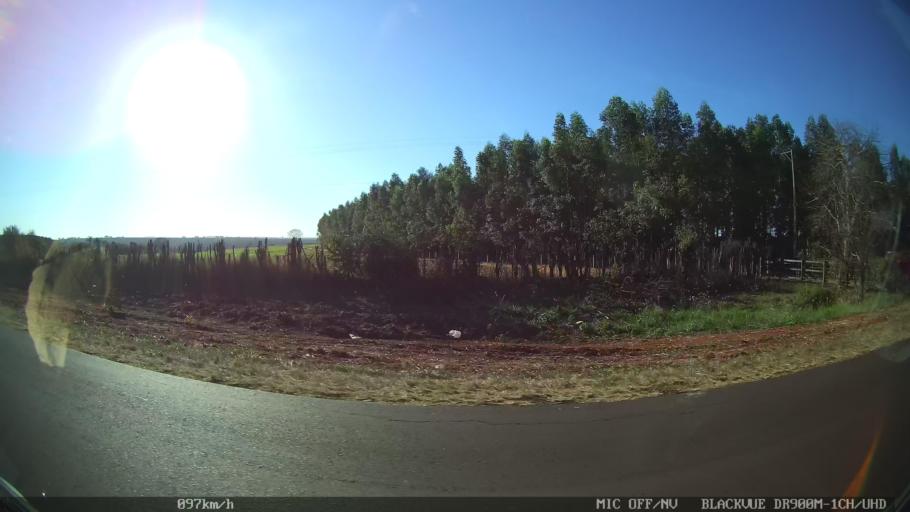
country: BR
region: Sao Paulo
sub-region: Guapiacu
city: Guapiacu
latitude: -20.7497
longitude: -49.1322
